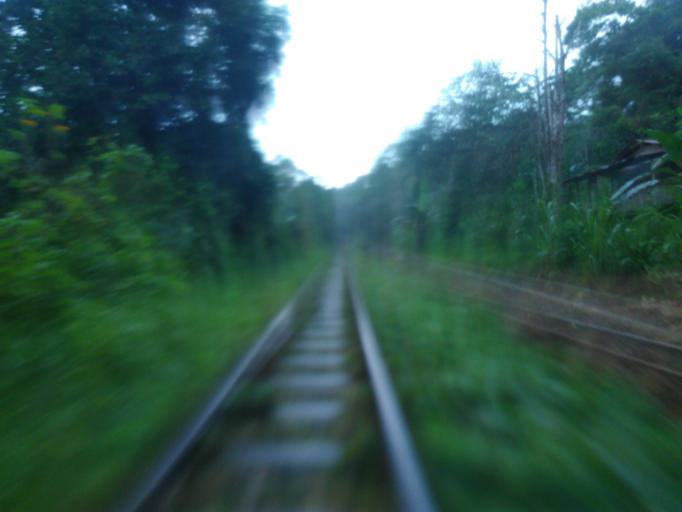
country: CO
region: Valle del Cauca
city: Buenaventura
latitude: 3.8499
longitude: -76.8603
